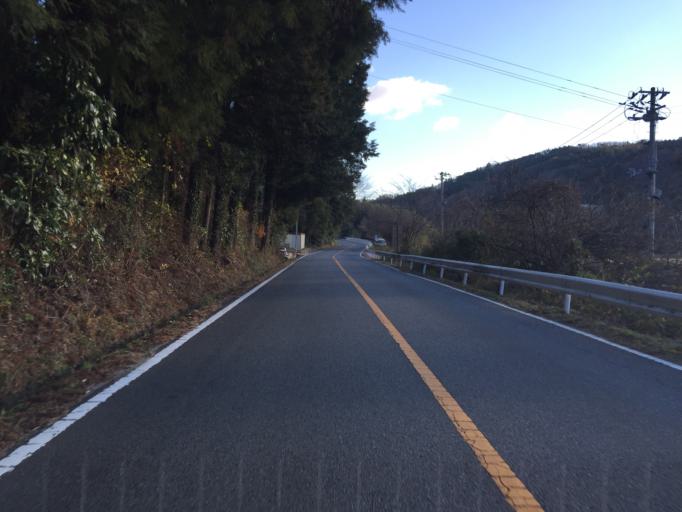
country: JP
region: Fukushima
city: Iwaki
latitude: 37.1482
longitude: 140.8329
